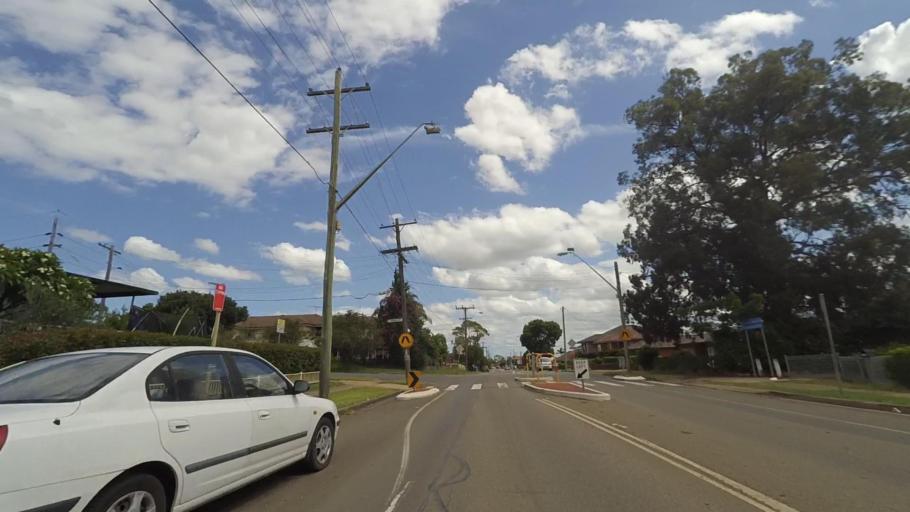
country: AU
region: New South Wales
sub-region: Holroyd
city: Guildford West
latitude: -33.8477
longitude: 150.9619
